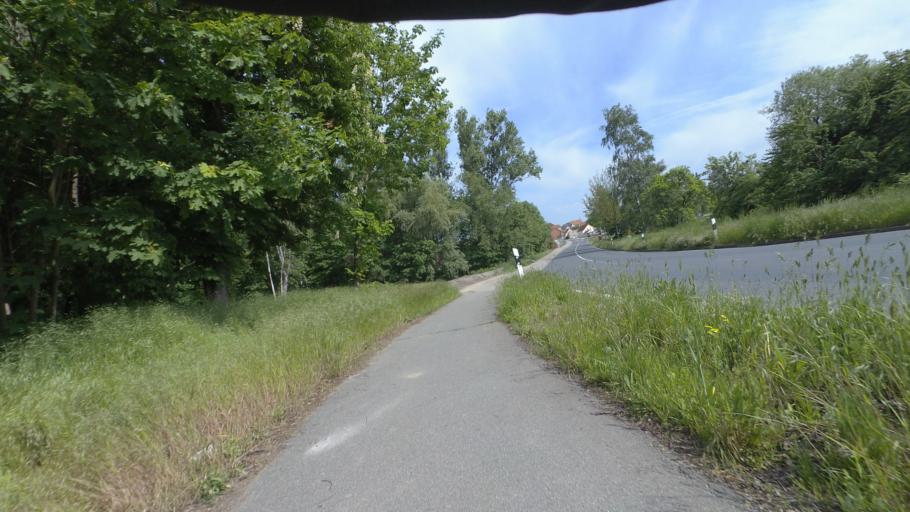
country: DE
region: Saxony-Anhalt
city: Hotensleben
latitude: 52.1235
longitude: 11.0106
